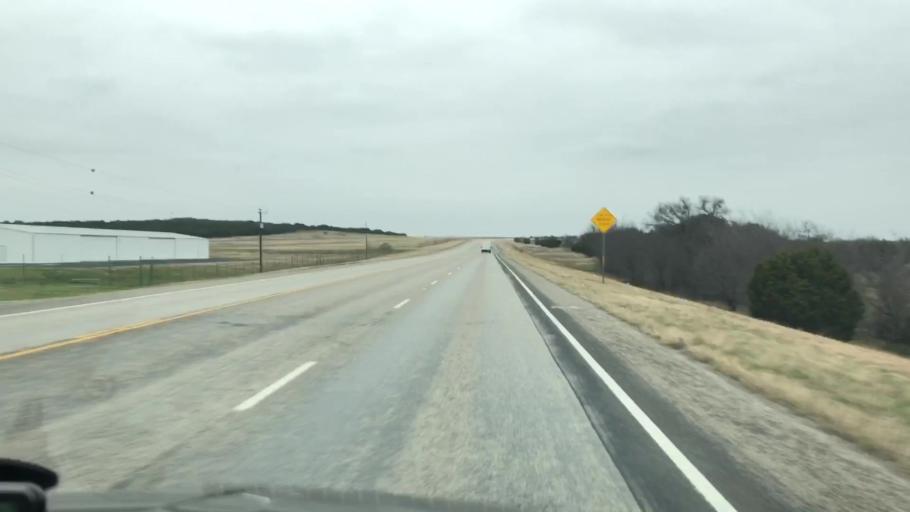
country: US
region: Texas
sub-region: Lampasas County
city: Lampasas
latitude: 31.1039
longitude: -98.1938
